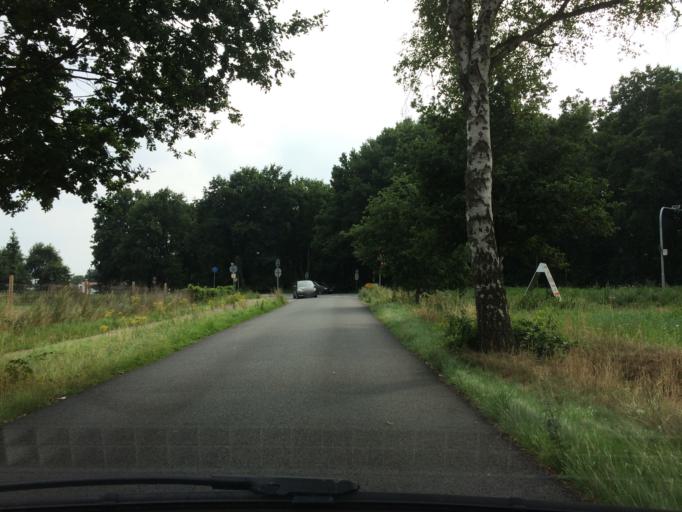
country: DE
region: North Rhine-Westphalia
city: Dorsten
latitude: 51.6898
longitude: 6.9491
